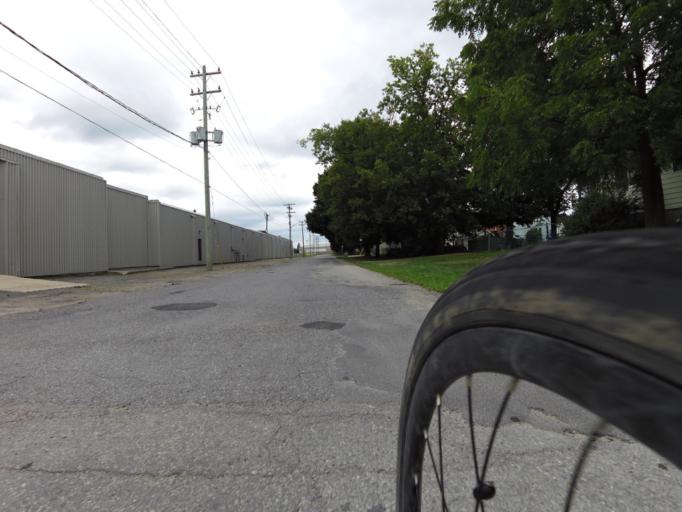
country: CA
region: Ontario
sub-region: Lanark County
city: Smiths Falls
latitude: 44.9020
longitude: -76.0265
